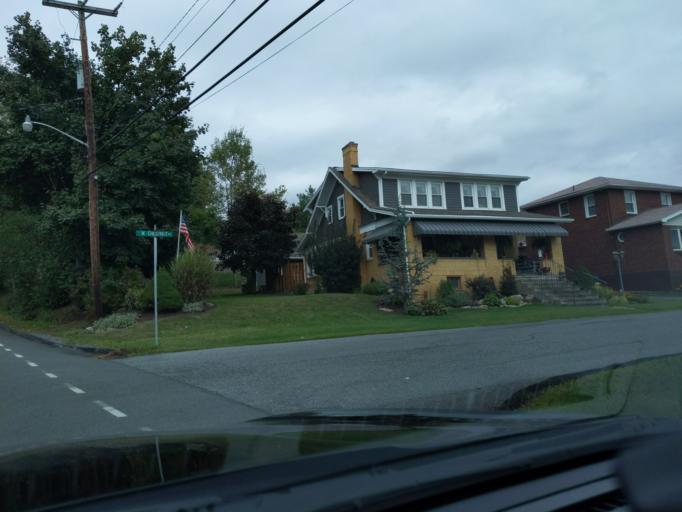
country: US
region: Pennsylvania
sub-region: Blair County
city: Lakemont
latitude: 40.4871
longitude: -78.4227
